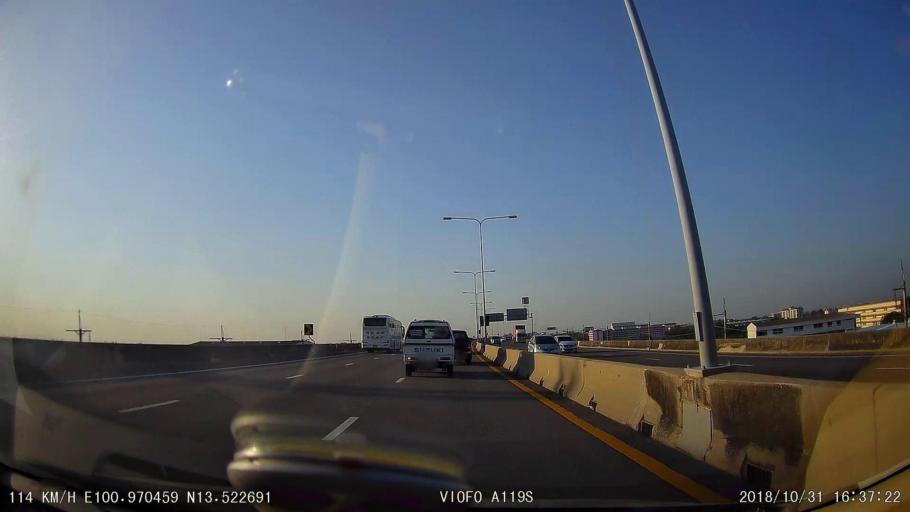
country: TH
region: Chachoengsao
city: Bang Pakong
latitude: 13.5234
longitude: 100.9702
